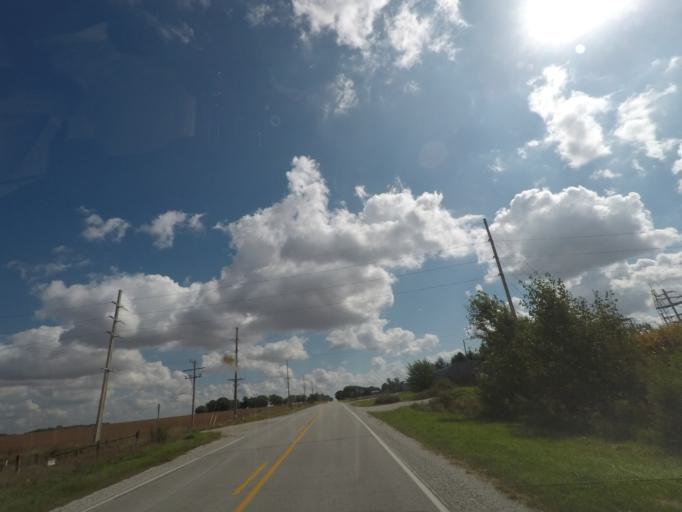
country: US
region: Iowa
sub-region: Story County
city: Nevada
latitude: 42.0225
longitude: -93.3294
